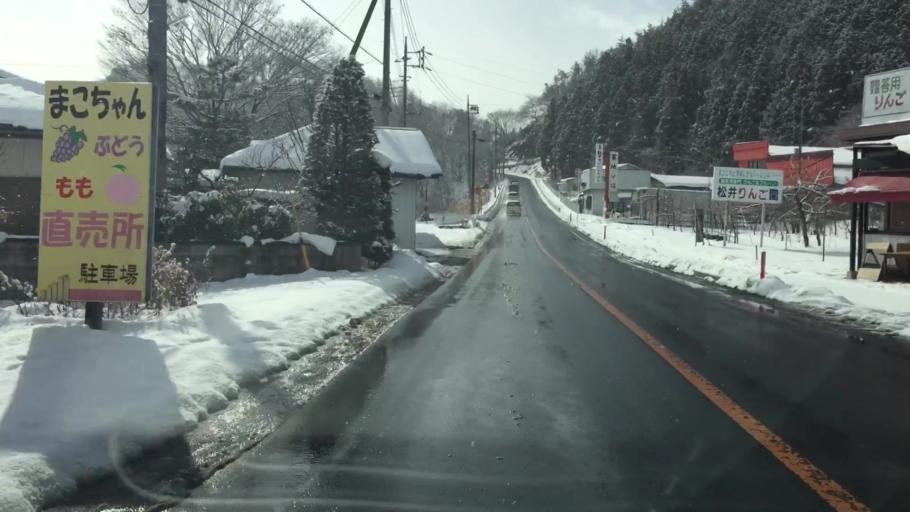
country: JP
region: Gunma
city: Numata
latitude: 36.6847
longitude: 139.0631
